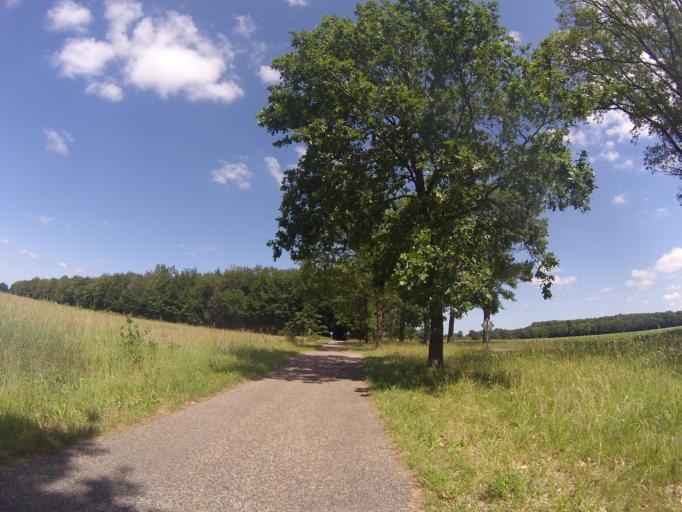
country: NL
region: Drenthe
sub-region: Gemeente Borger-Odoorn
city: Borger
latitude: 52.8672
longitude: 6.8588
